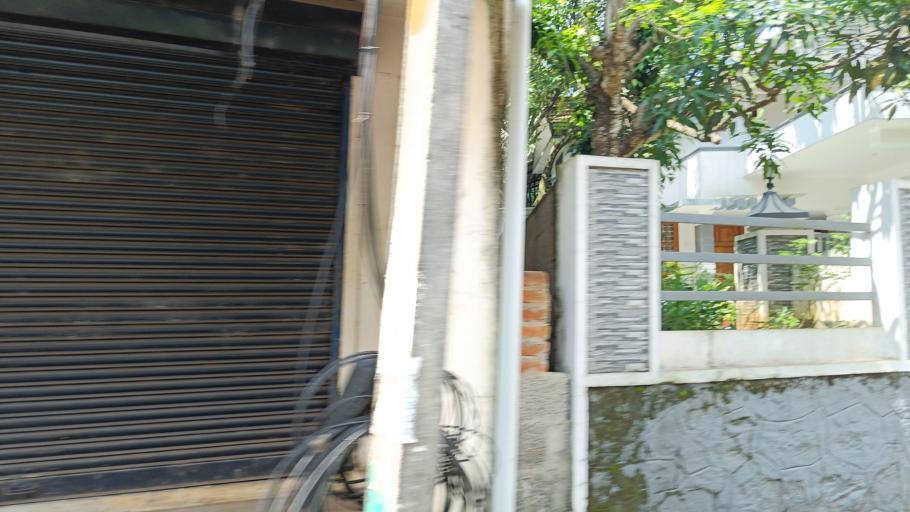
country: IN
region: Kerala
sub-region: Kottayam
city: Erattupetta
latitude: 9.5243
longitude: 76.8291
